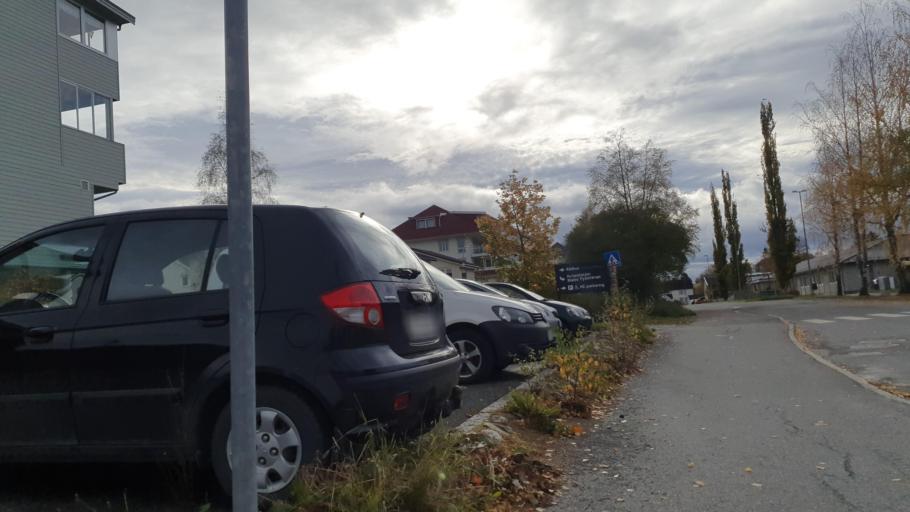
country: NO
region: Sor-Trondelag
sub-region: Klaebu
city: Klaebu
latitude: 63.3005
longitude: 10.4832
